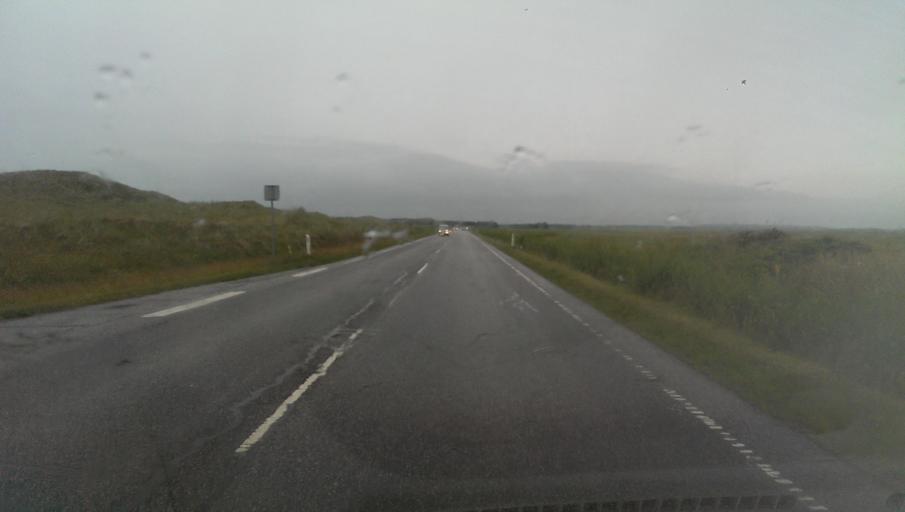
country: DK
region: Central Jutland
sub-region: Ringkobing-Skjern Kommune
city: Ringkobing
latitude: 56.2330
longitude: 8.1392
